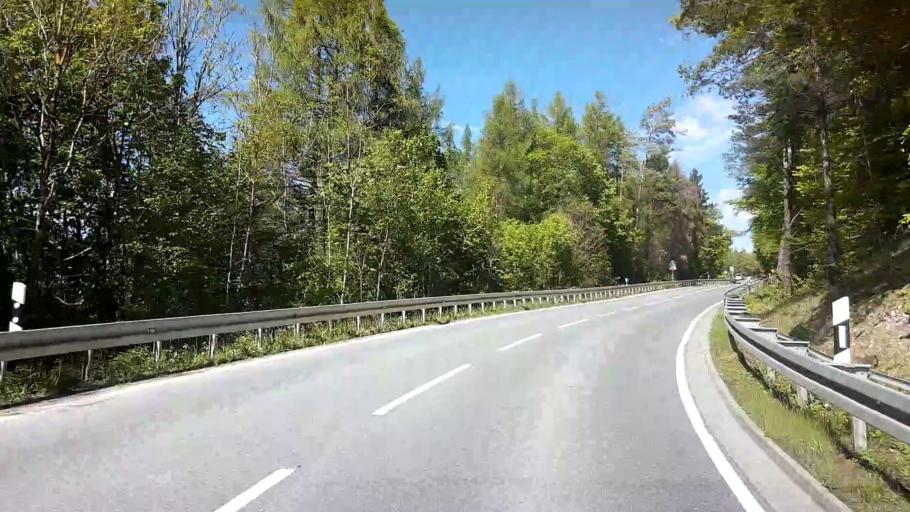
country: DE
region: Bavaria
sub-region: Upper Franconia
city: Weilersbach
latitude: 49.8074
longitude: 11.1277
